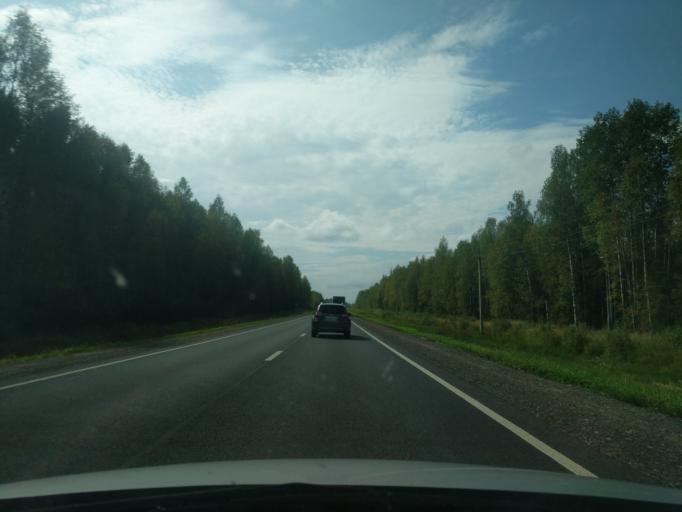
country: RU
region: Kostroma
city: Kadyy
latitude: 57.8054
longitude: 43.2150
